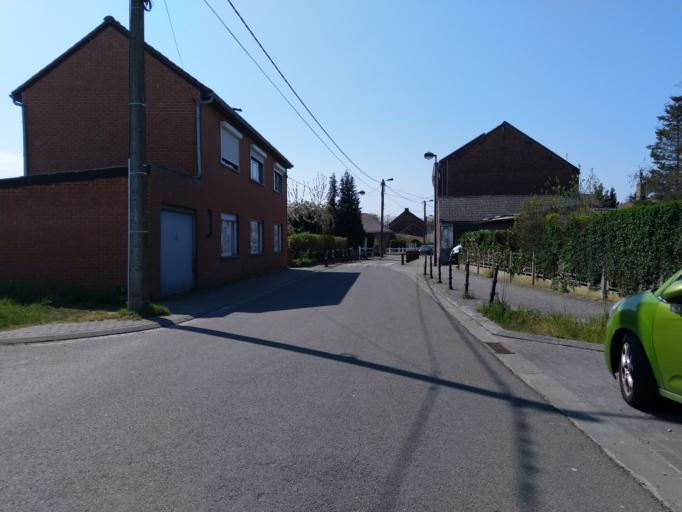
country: BE
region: Wallonia
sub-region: Province du Hainaut
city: Mons
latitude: 50.4809
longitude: 3.9182
